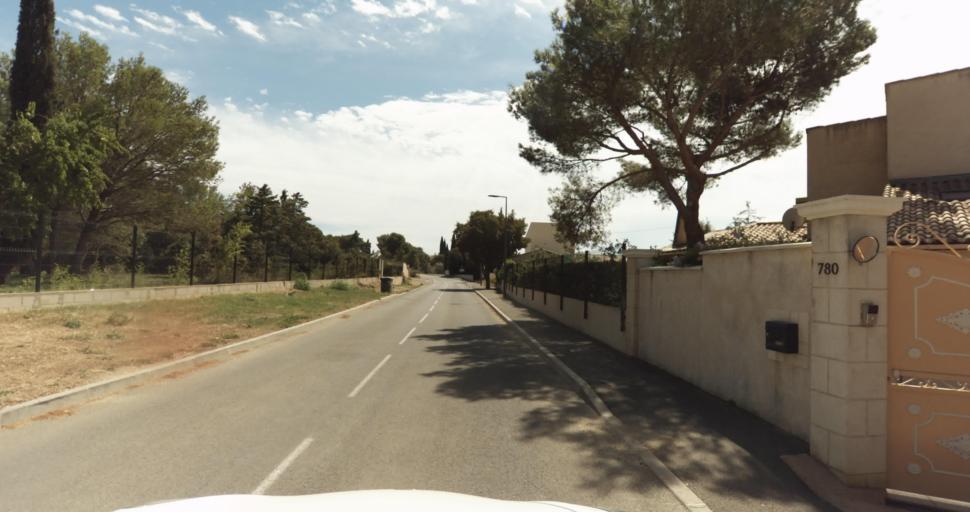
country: FR
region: Provence-Alpes-Cote d'Azur
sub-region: Departement des Bouches-du-Rhone
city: Miramas
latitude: 43.5811
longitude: 5.0215
